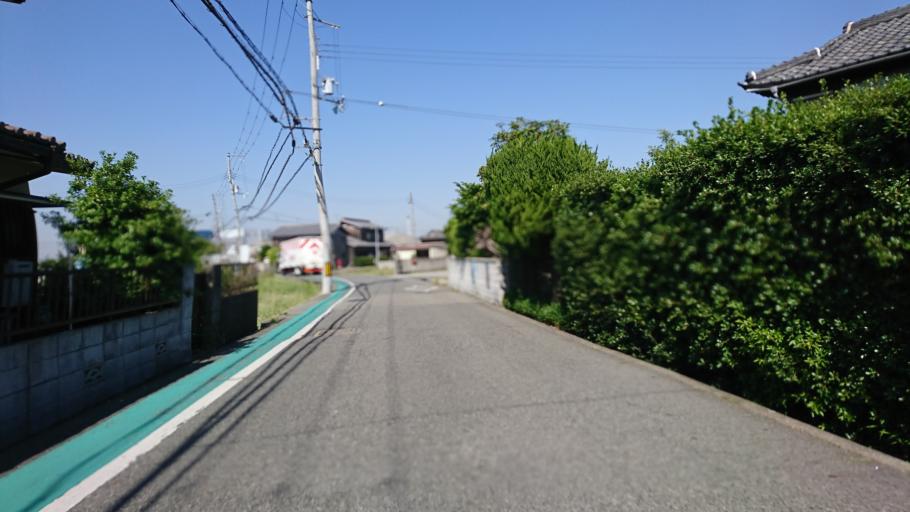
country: JP
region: Hyogo
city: Kakogawacho-honmachi
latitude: 34.7582
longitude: 134.8706
